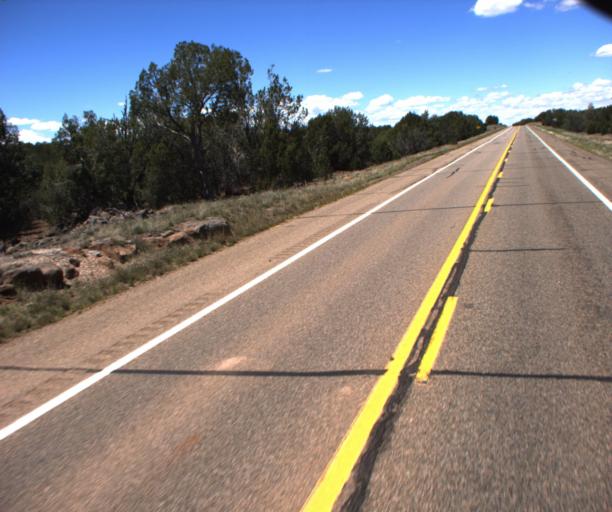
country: US
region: Arizona
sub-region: Yavapai County
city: Paulden
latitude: 35.1332
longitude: -112.4397
